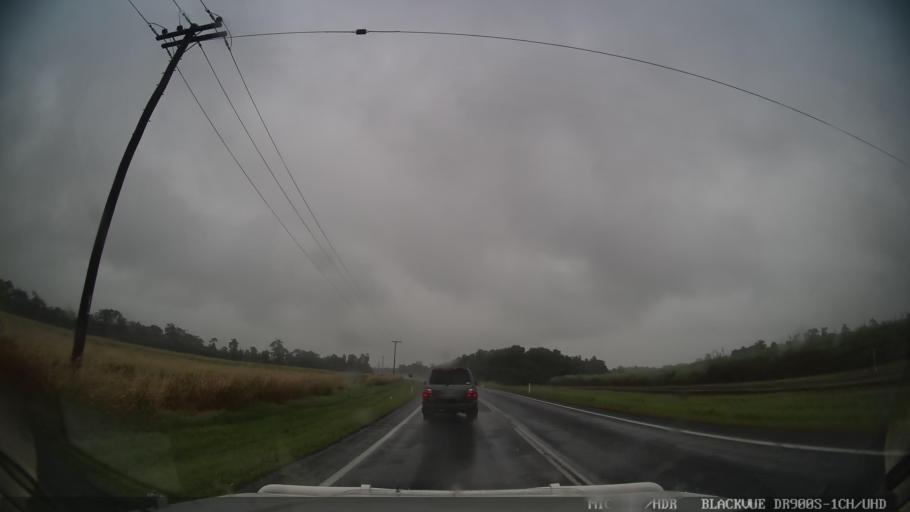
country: AU
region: Queensland
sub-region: Cassowary Coast
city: Innisfail
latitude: -17.6579
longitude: 146.0367
